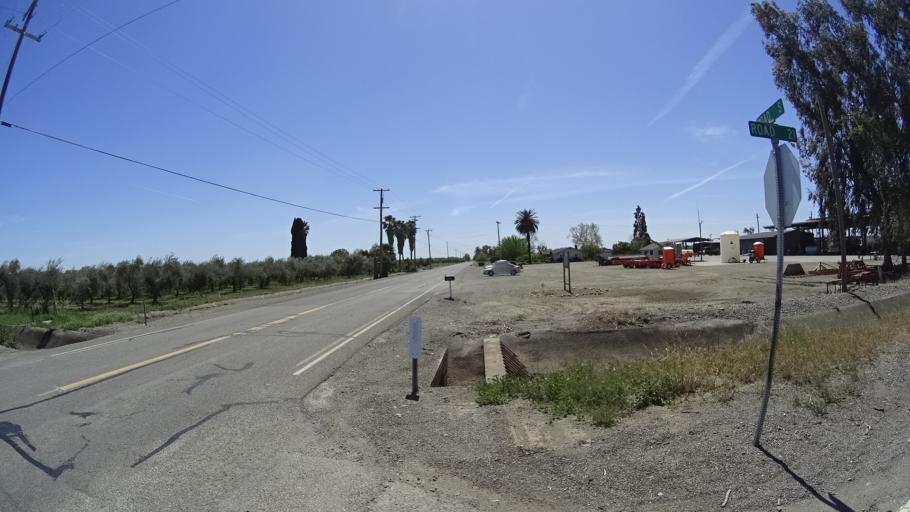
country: US
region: California
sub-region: Glenn County
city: Hamilton City
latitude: 39.7212
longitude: -122.1045
